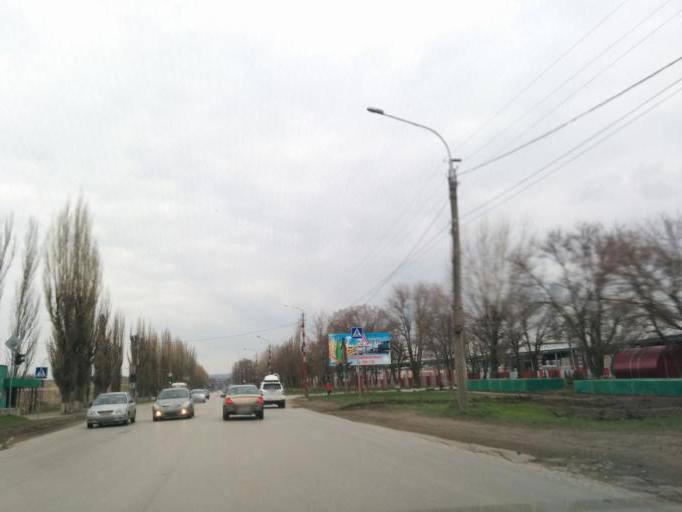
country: RU
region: Rostov
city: Novocherkassk
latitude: 47.4750
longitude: 40.1017
